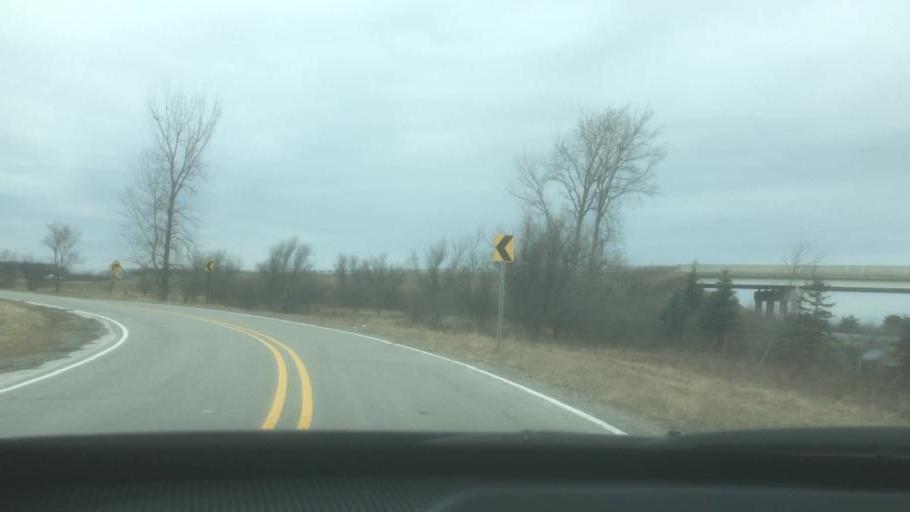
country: US
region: Michigan
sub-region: Bay County
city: Bay City
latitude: 43.6229
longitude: -83.9554
